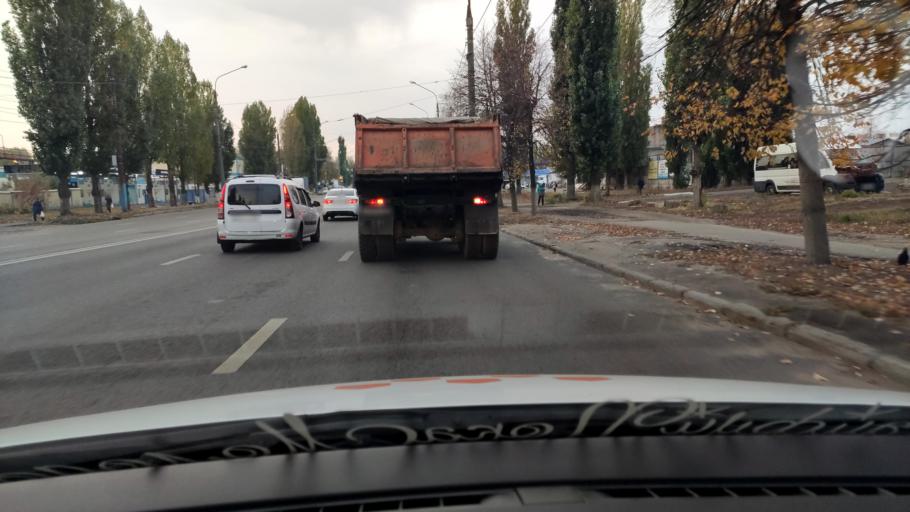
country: RU
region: Voronezj
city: Voronezh
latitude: 51.6835
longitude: 39.1657
